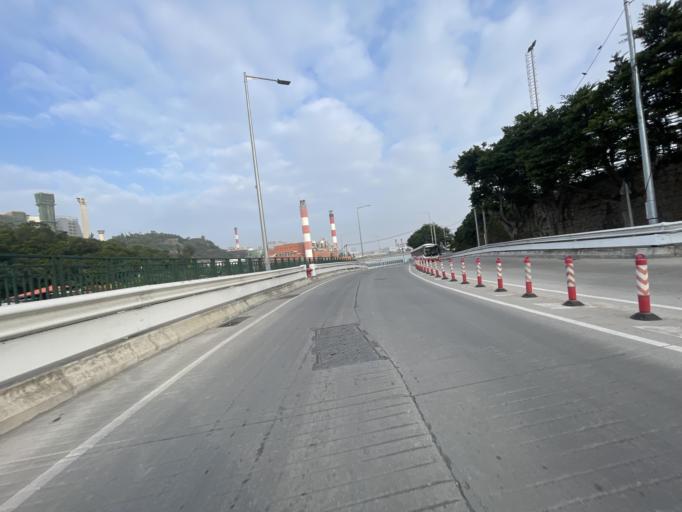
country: MO
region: Macau
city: Macau
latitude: 22.1341
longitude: 113.5816
